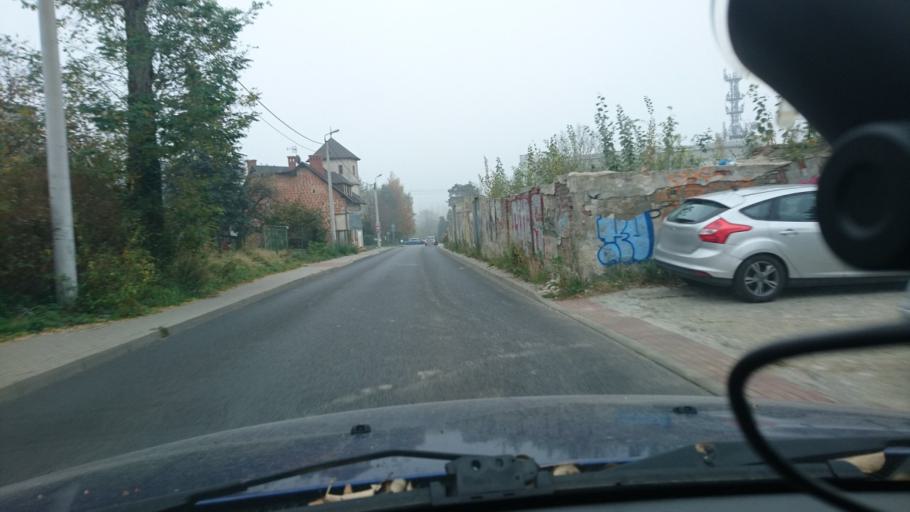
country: PL
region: Silesian Voivodeship
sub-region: Bielsko-Biala
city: Bielsko-Biala
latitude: 49.8189
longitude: 19.0319
